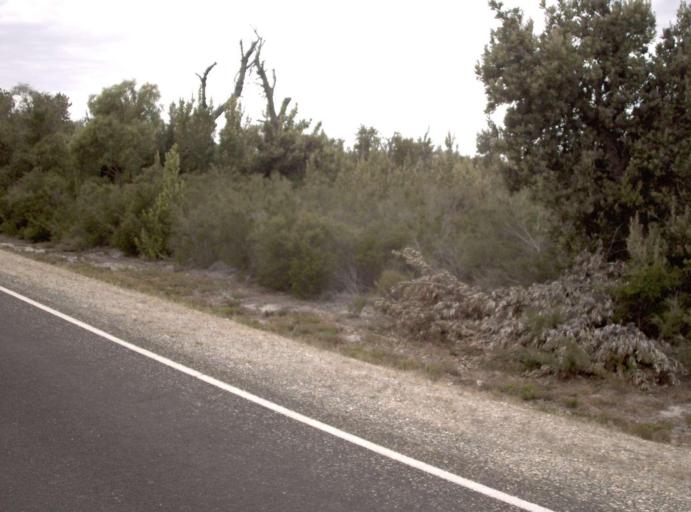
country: AU
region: Victoria
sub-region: Wellington
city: Sale
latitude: -38.1940
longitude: 147.3639
